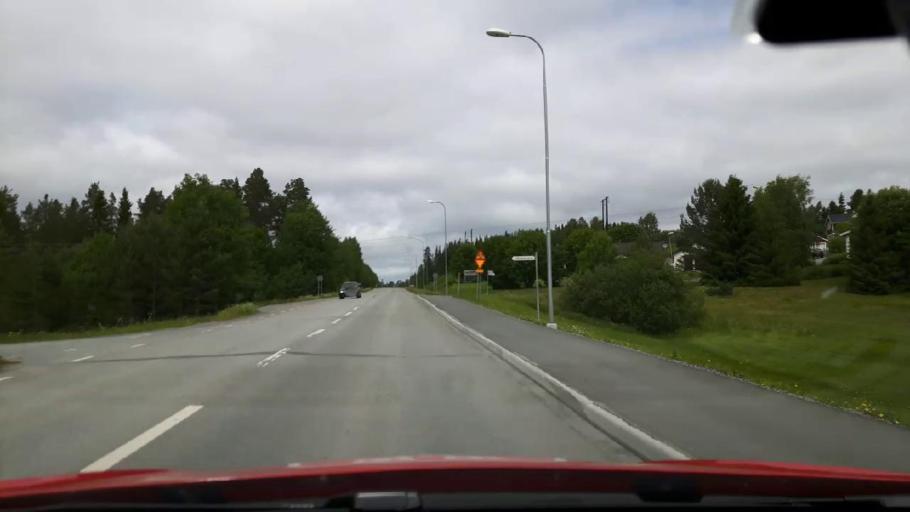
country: SE
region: Jaemtland
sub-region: Krokoms Kommun
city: Krokom
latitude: 63.3346
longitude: 14.4449
